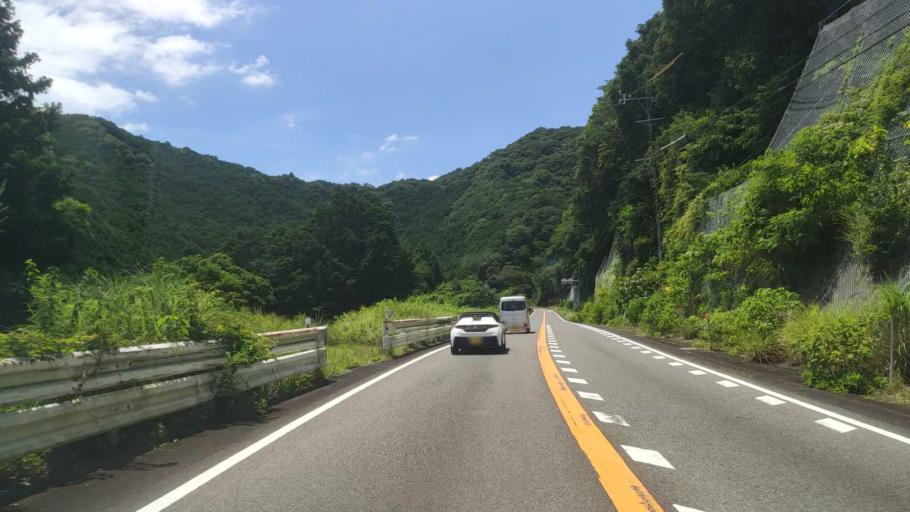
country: JP
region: Mie
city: Owase
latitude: 34.1590
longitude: 136.2705
